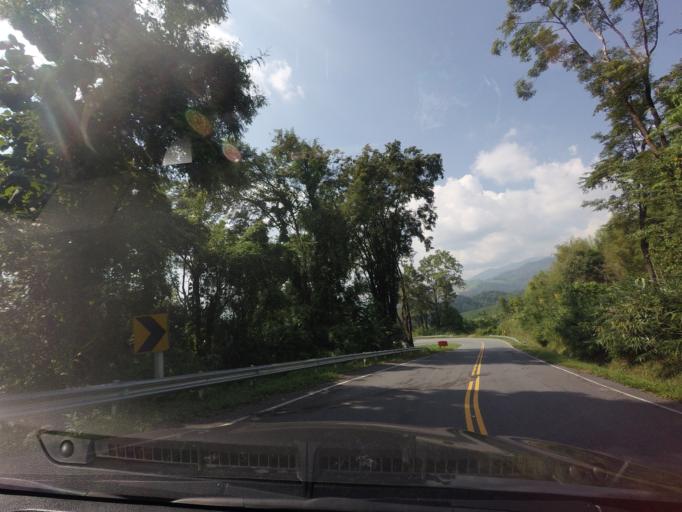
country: TH
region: Nan
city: Santi Suk
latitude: 18.9758
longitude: 100.9919
